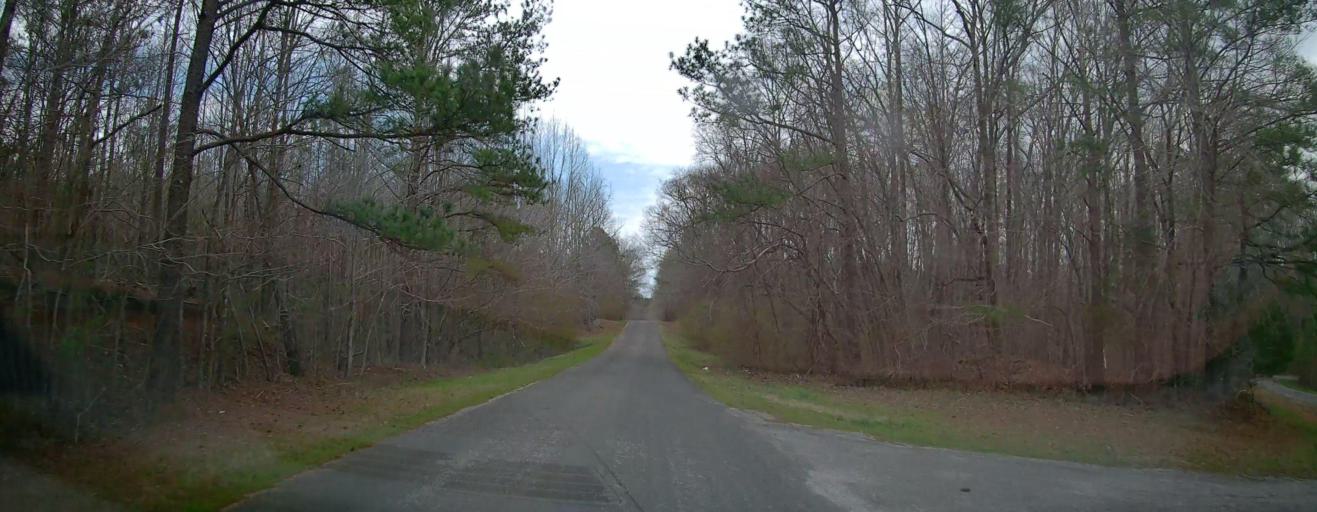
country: US
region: Alabama
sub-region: Marion County
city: Hamilton
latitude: 34.1996
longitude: -88.1804
